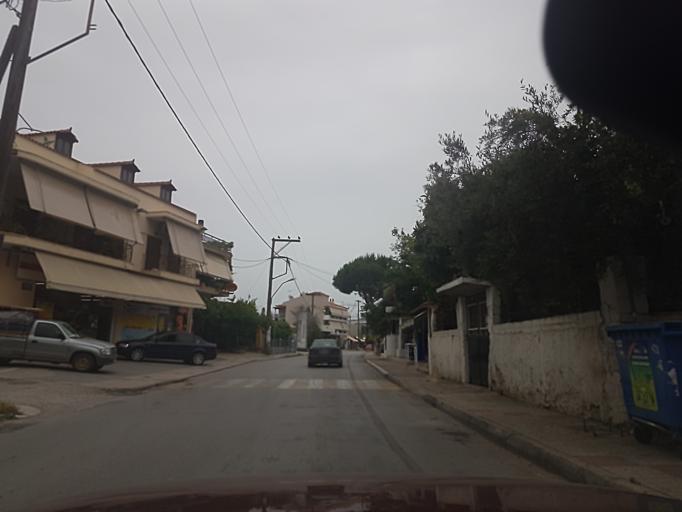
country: GR
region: Central Greece
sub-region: Nomos Evvoias
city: Chalkida
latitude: 38.4667
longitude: 23.6197
